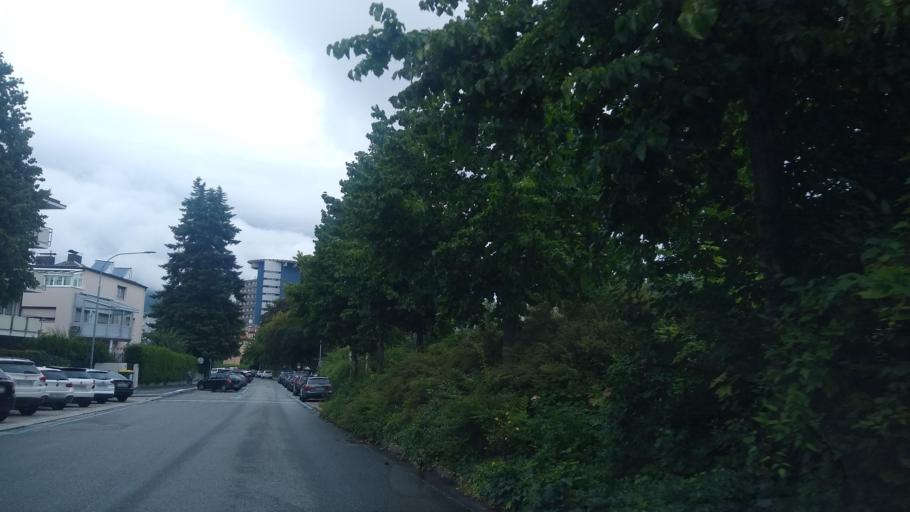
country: AT
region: Tyrol
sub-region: Innsbruck Stadt
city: Innsbruck
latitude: 47.2579
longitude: 11.3832
